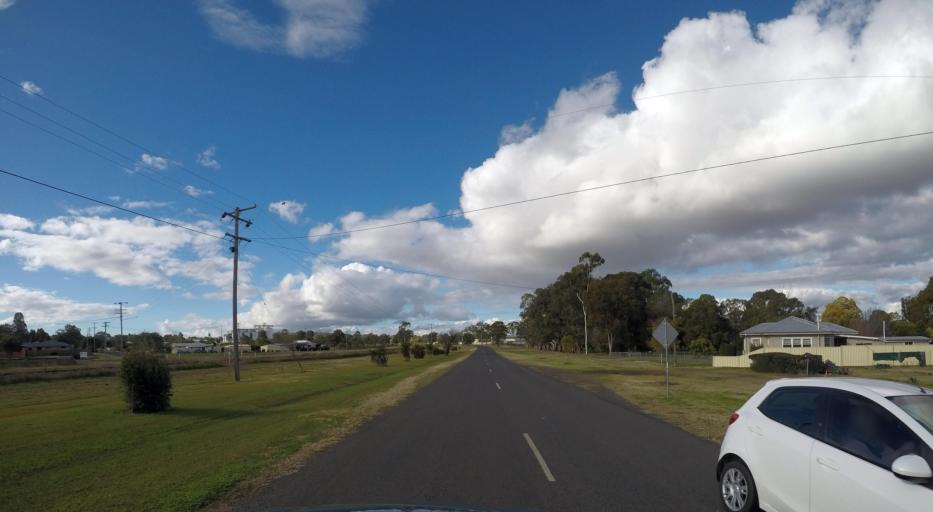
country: AU
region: Queensland
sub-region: Toowoomba
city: Westbrook
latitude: -27.7134
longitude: 151.6380
